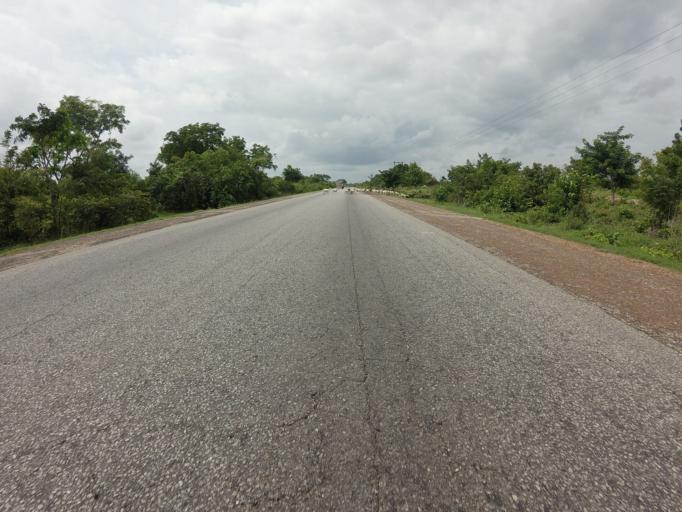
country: GH
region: Brong-Ahafo
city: Kintampo
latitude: 8.7443
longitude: -1.4642
